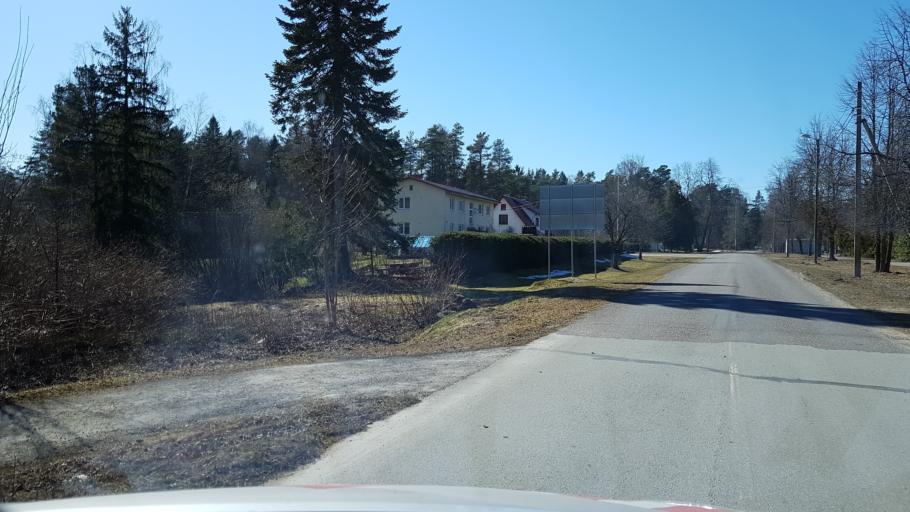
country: EE
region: Ida-Virumaa
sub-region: Aseri vald
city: Aseri
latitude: 59.3511
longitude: 26.8202
